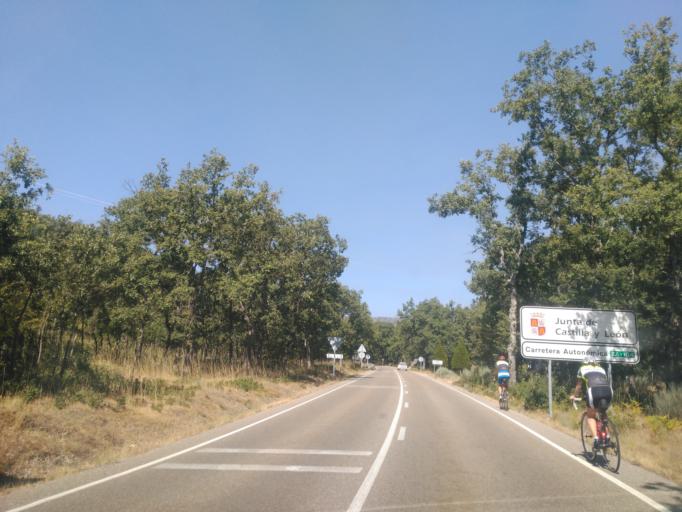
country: ES
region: Castille and Leon
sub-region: Provincia de Zamora
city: Galende
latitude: 42.1175
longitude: -6.6905
